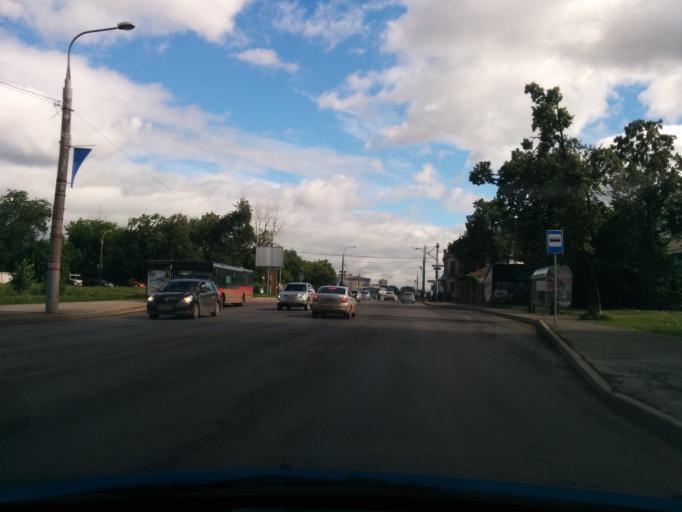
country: RU
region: Perm
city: Perm
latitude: 58.0147
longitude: 56.2235
